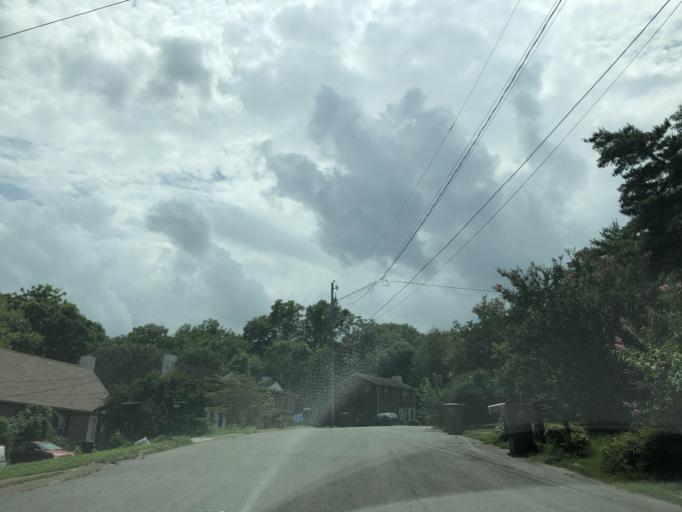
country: US
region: Tennessee
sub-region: Williamson County
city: Brentwood Estates
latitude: 36.0609
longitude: -86.6931
